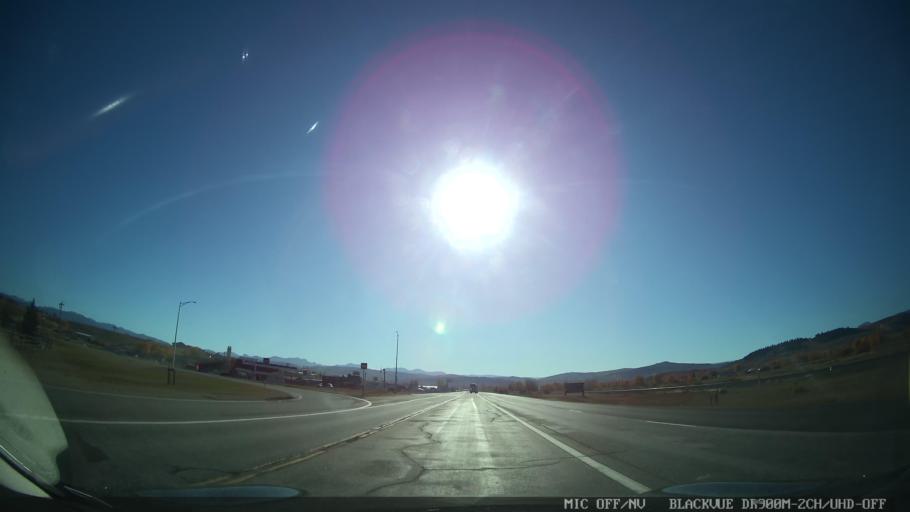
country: US
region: Colorado
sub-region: Grand County
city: Granby
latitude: 40.0908
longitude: -105.9592
